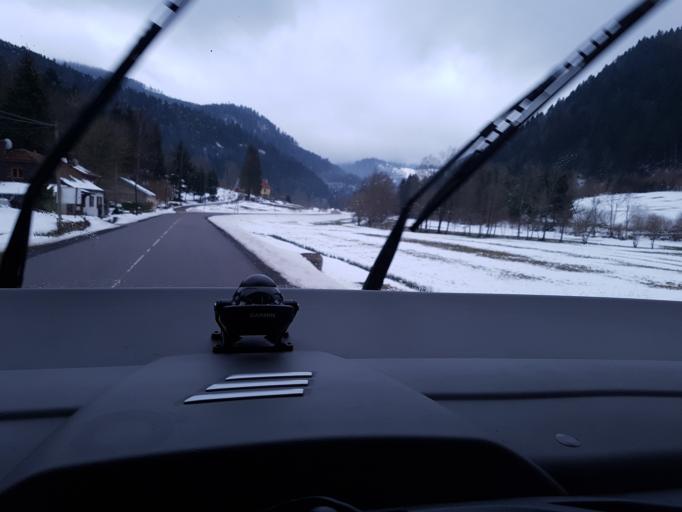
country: FR
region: Lorraine
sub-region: Departement des Vosges
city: Plainfaing
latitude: 48.1412
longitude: 7.0229
